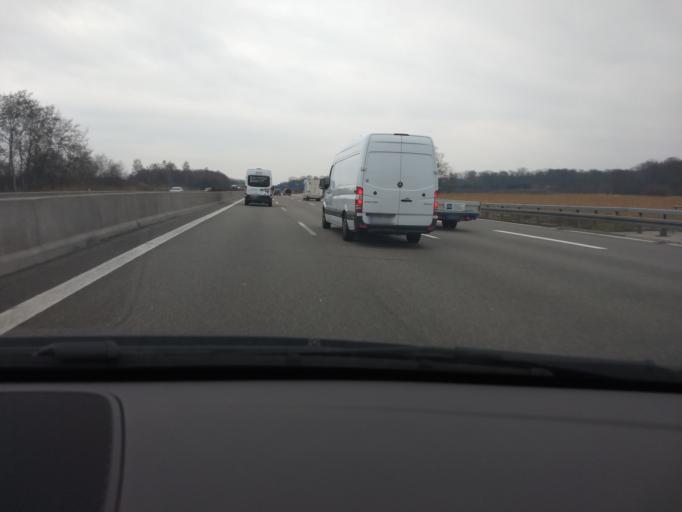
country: DE
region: Baden-Wuerttemberg
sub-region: Freiburg Region
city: Willstatt
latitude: 48.5299
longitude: 7.9294
